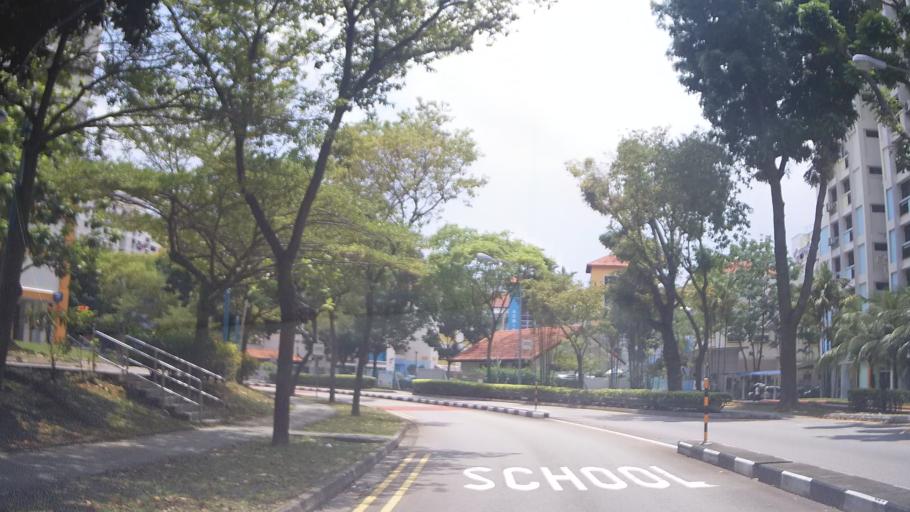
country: MY
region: Johor
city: Johor Bahru
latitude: 1.4423
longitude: 103.7990
